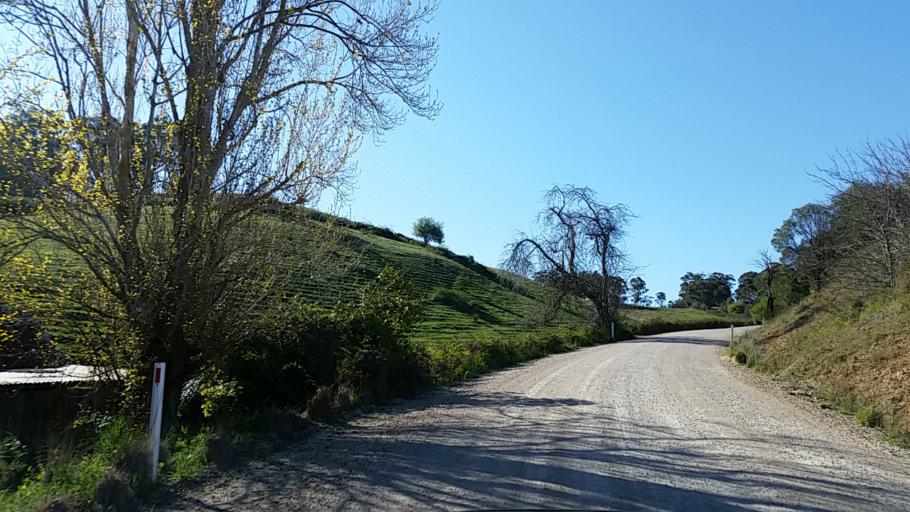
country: AU
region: South Australia
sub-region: Adelaide Hills
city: Lobethal
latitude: -34.8909
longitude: 138.8554
